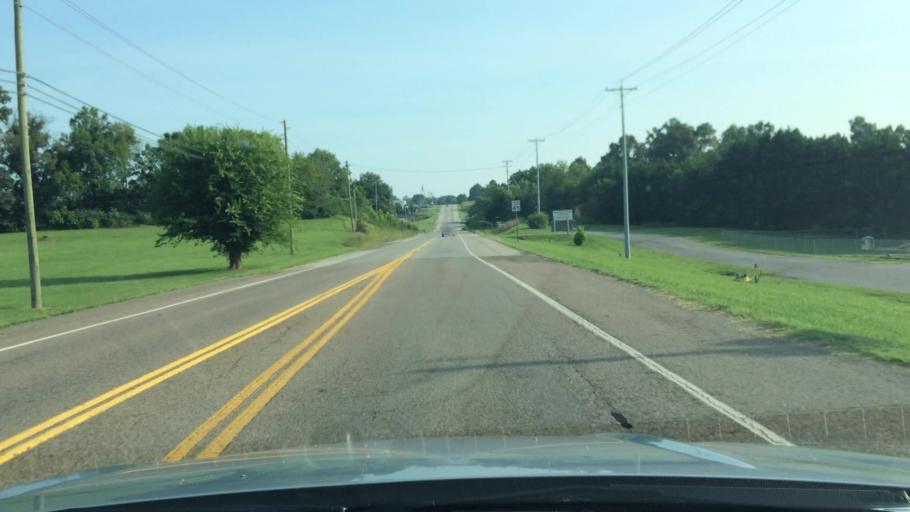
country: US
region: Tennessee
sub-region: Blount County
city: Maryville
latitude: 35.7462
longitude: -84.0443
